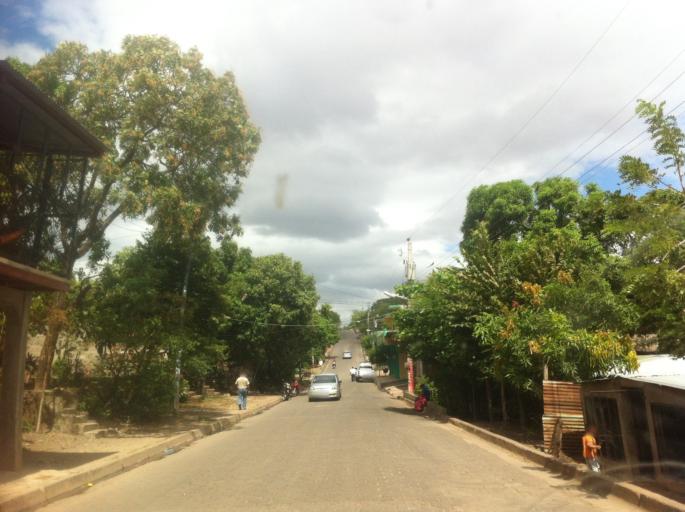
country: NI
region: Chontales
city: Juigalpa
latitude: 12.0971
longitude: -85.3606
